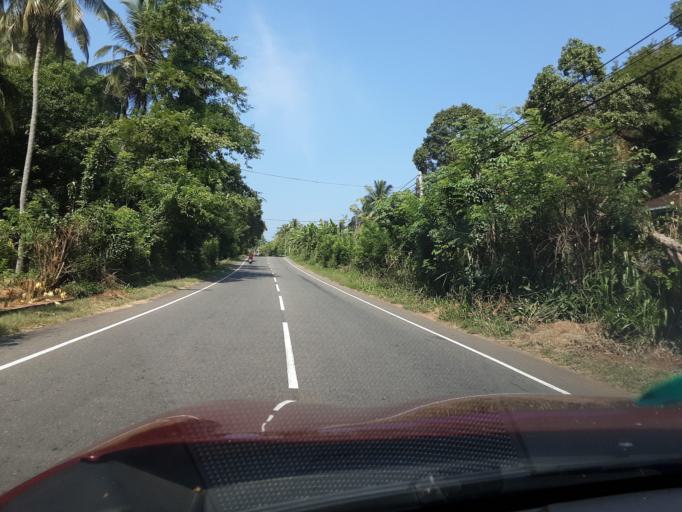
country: LK
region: Uva
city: Badulla
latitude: 7.1883
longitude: 81.0368
